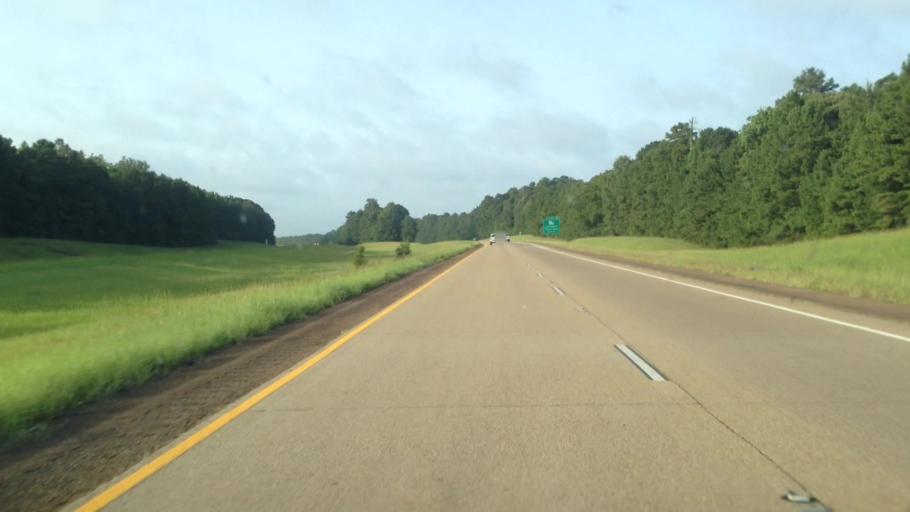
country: US
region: Louisiana
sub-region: Rapides Parish
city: Lecompte
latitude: 31.1045
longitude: -92.4452
